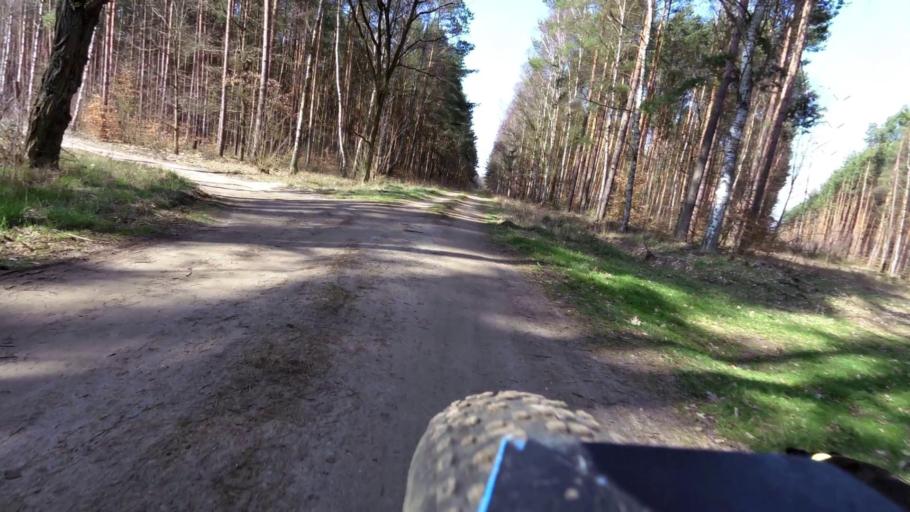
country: PL
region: Lubusz
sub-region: Powiat slubicki
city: Cybinka
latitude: 52.2127
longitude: 14.8586
